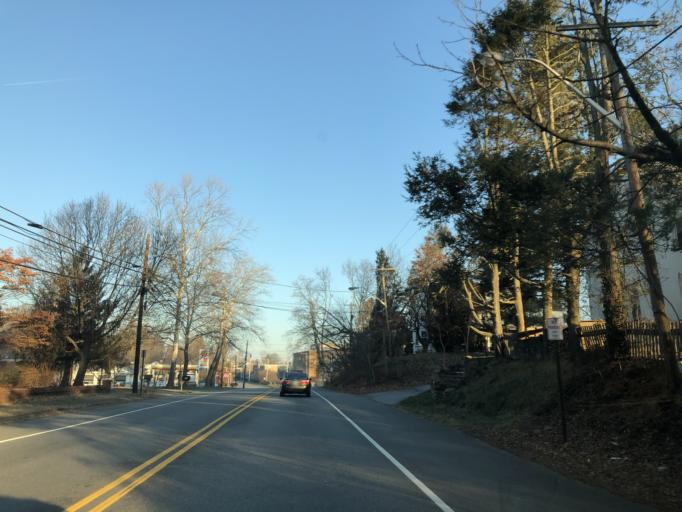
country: US
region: Pennsylvania
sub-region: Chester County
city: West Chester
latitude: 39.9484
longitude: -75.5937
